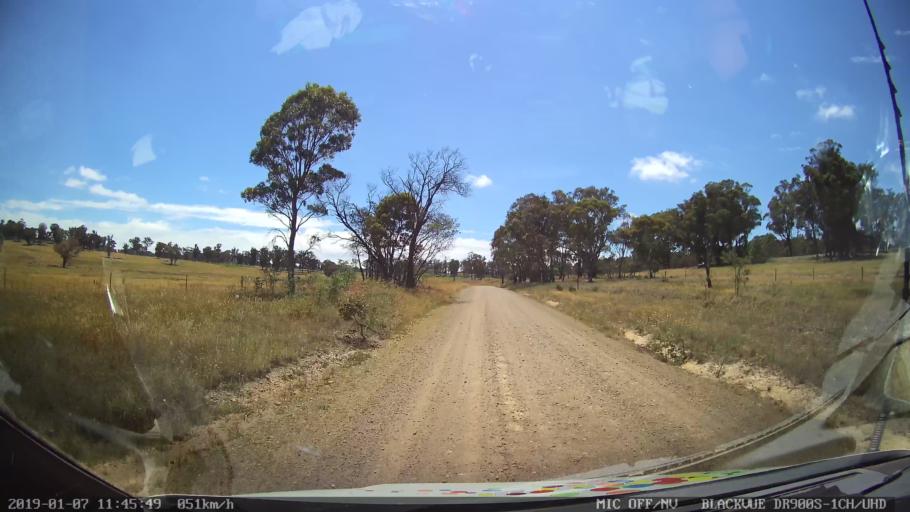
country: AU
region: New South Wales
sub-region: Guyra
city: Guyra
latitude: -30.3449
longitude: 151.6085
